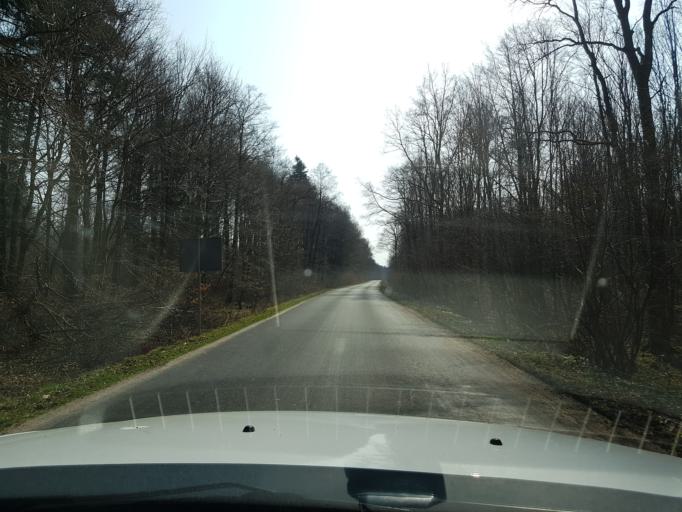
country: PL
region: West Pomeranian Voivodeship
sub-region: Powiat koszalinski
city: Sianow
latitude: 54.2713
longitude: 16.3140
